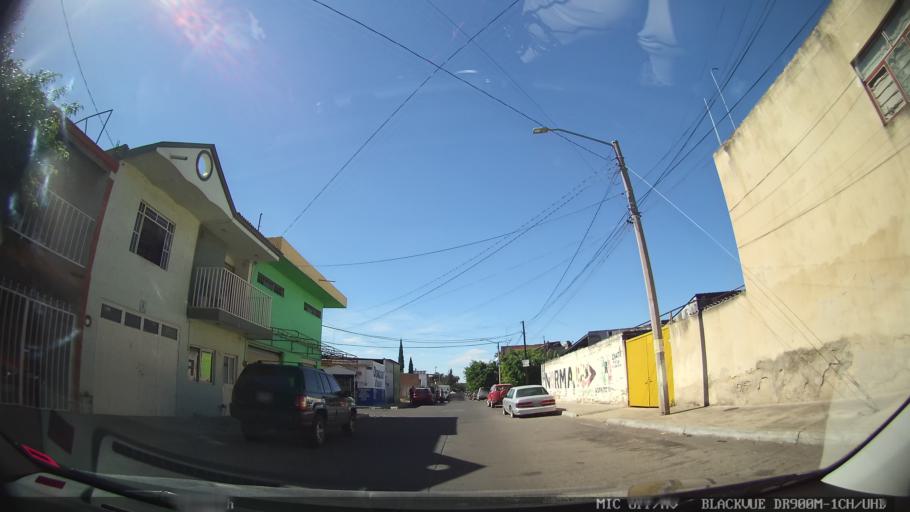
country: MX
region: Jalisco
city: Tlaquepaque
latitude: 20.6595
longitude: -103.2855
